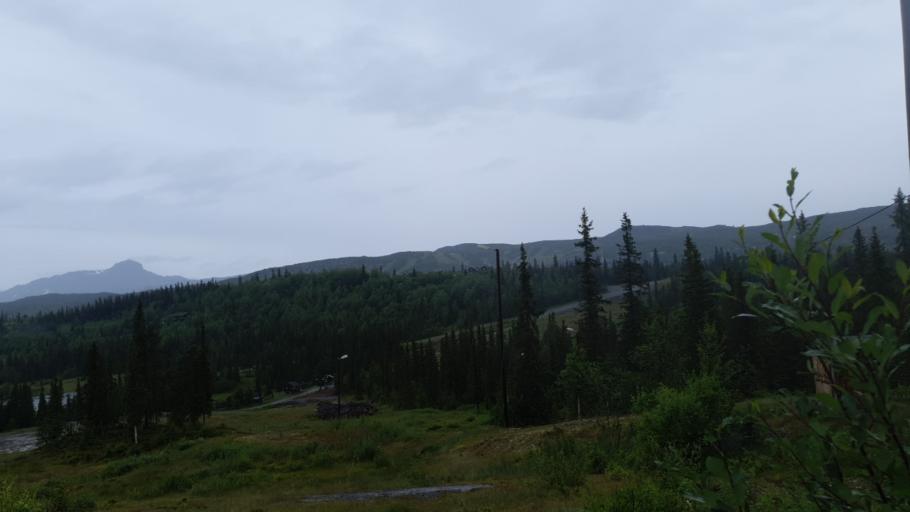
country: NO
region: Oppland
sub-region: Vestre Slidre
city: Slidre
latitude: 61.2309
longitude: 8.9120
